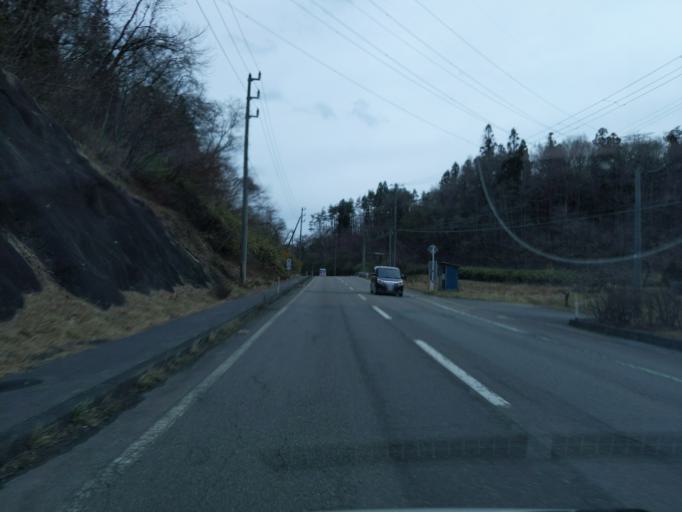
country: JP
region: Iwate
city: Mizusawa
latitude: 39.0312
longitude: 141.3032
